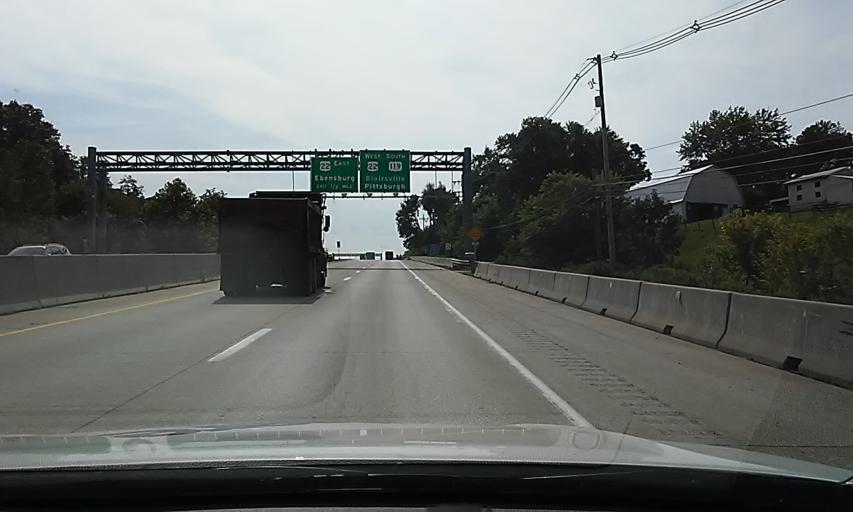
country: US
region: Pennsylvania
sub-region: Indiana County
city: Black Lick
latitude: 40.4510
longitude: -79.2133
